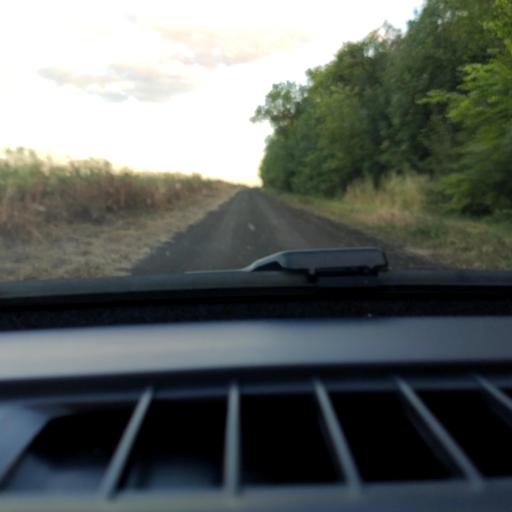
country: RU
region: Voronezj
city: Verkhnyaya Khava
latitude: 51.6053
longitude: 39.8375
